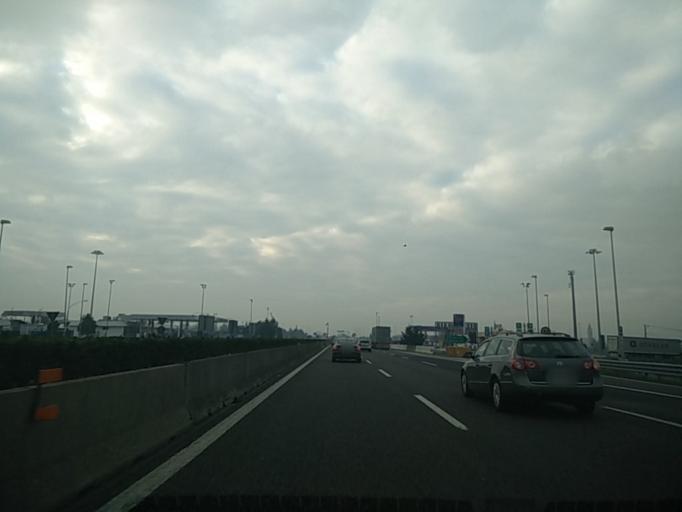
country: IT
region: Emilia-Romagna
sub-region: Forli-Cesena
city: San Mauro Pascoli
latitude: 44.1162
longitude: 12.4106
